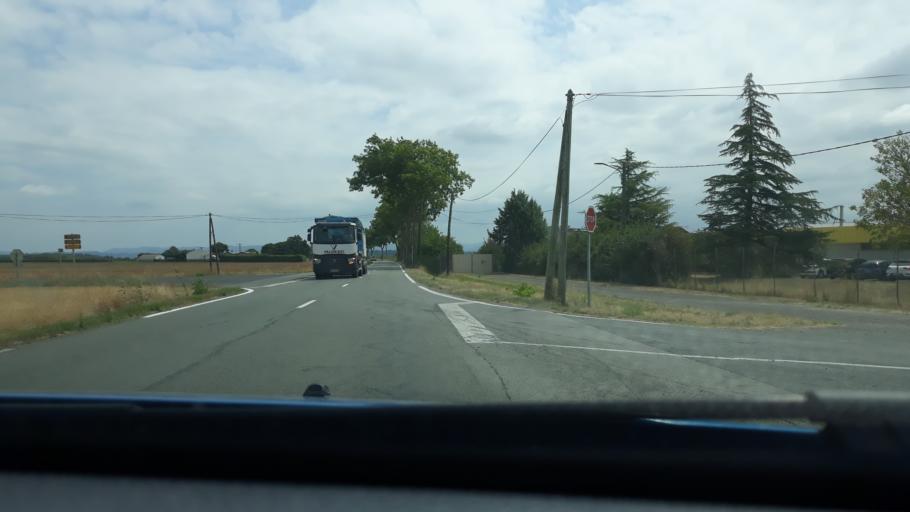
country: FR
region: Languedoc-Roussillon
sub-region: Departement de l'Aude
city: Pezens
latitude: 43.2649
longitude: 2.2424
